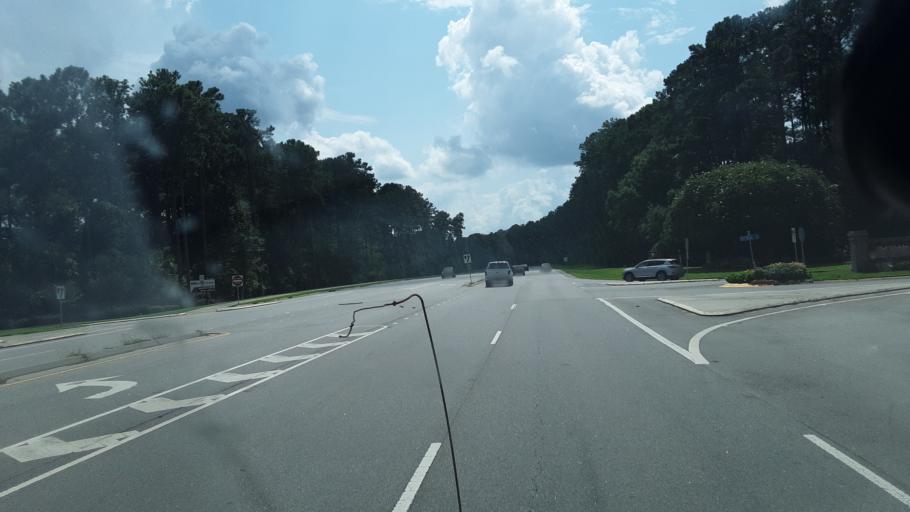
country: US
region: South Carolina
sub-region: Beaufort County
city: Bluffton
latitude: 32.2866
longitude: -80.9419
